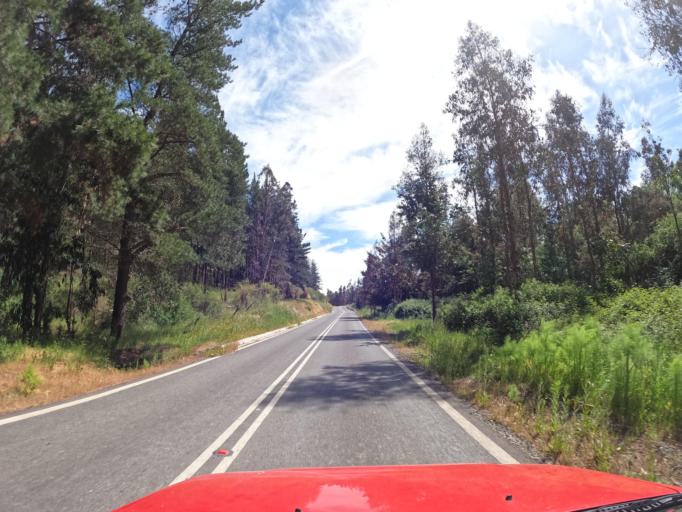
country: CL
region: Maule
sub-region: Provincia de Talca
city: Talca
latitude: -34.9931
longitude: -71.8726
